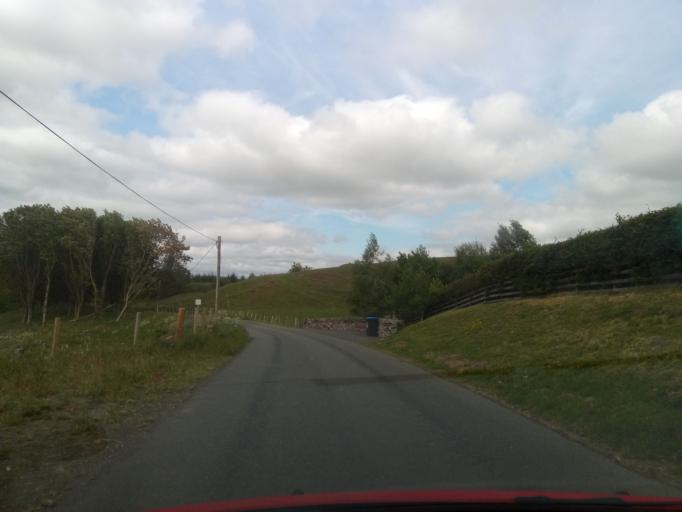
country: GB
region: Scotland
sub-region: The Scottish Borders
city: Selkirk
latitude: 55.5242
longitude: -2.8223
